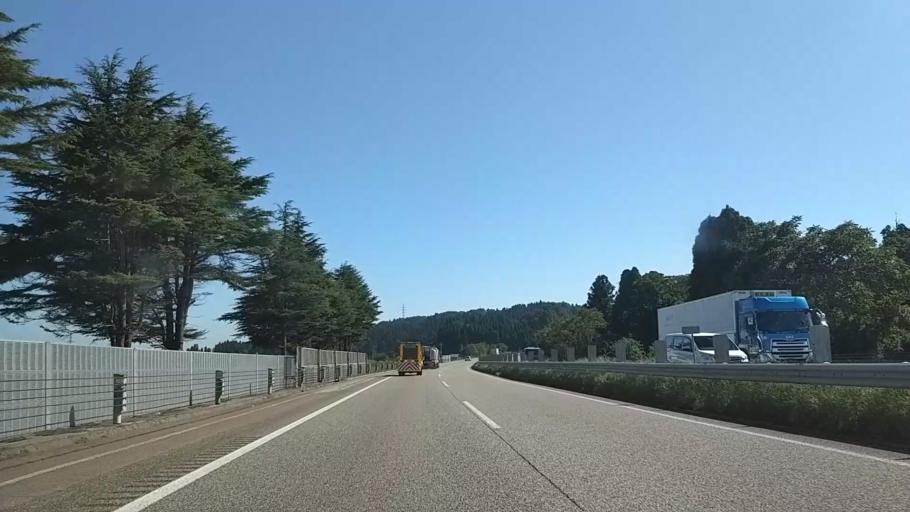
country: JP
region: Toyama
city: Takaoka
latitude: 36.6797
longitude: 137.0399
